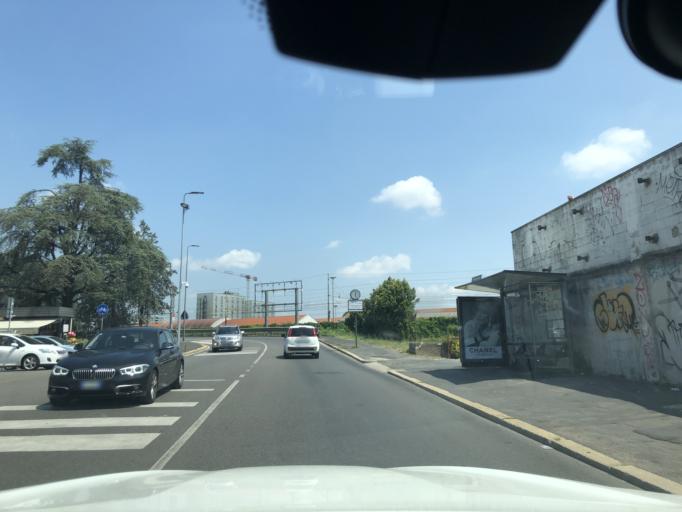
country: IT
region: Lombardy
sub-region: Citta metropolitana di Milano
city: Sesto San Giovanni
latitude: 45.5041
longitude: 9.2120
